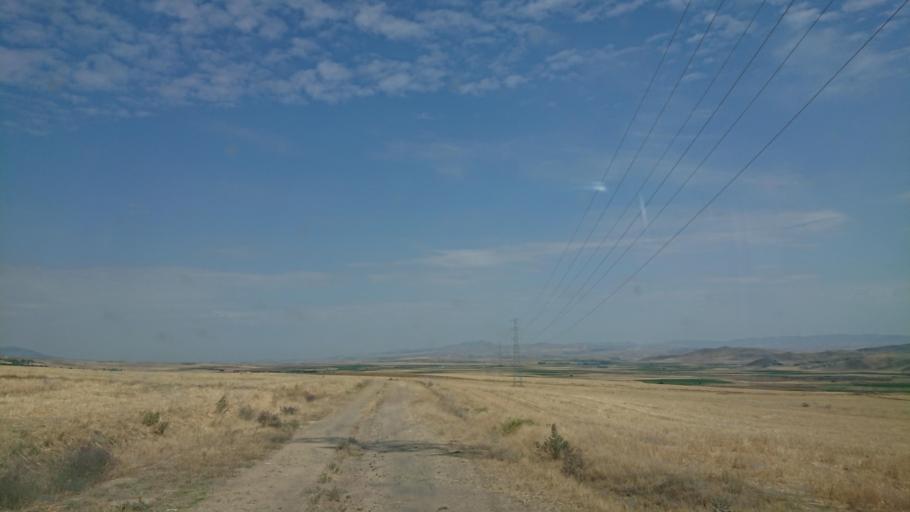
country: TR
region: Aksaray
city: Agacoren
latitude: 38.9508
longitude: 33.9115
